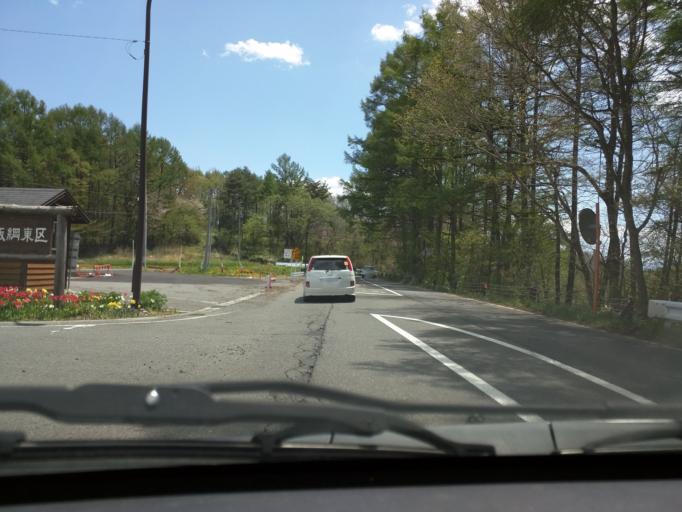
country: JP
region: Nagano
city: Nagano-shi
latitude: 36.7019
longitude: 138.1512
